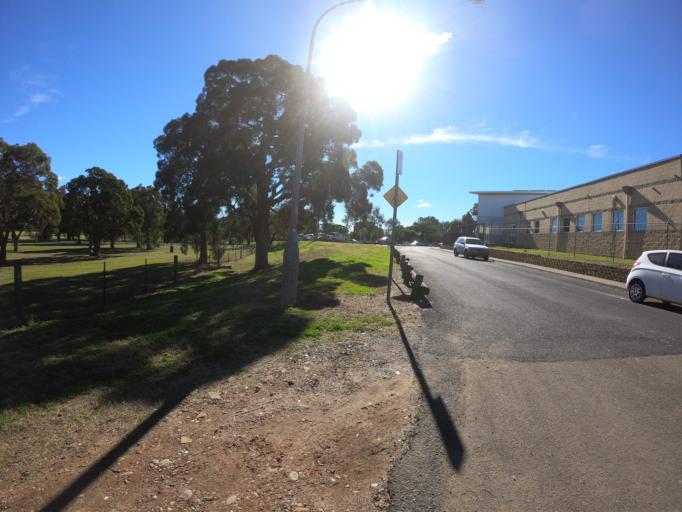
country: AU
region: New South Wales
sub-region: Hawkesbury
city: South Windsor
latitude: -33.6222
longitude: 150.8000
